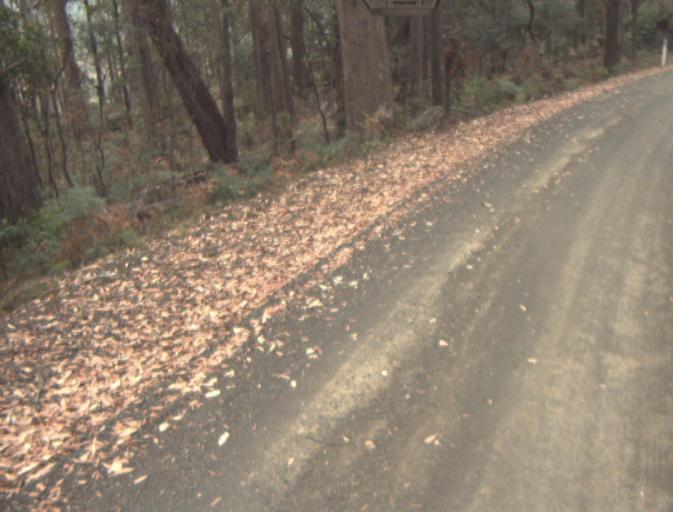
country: AU
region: Tasmania
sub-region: Northern Midlands
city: Evandale
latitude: -41.4941
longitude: 147.5489
